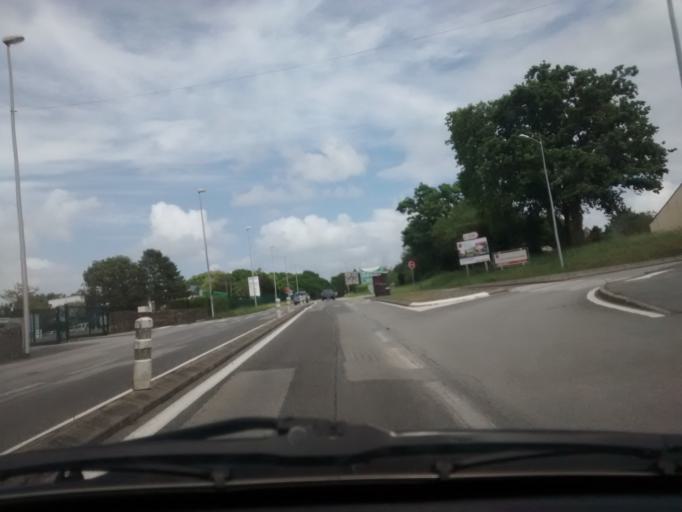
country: FR
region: Brittany
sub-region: Departement du Morbihan
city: Arradon
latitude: 47.6517
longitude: -2.7885
